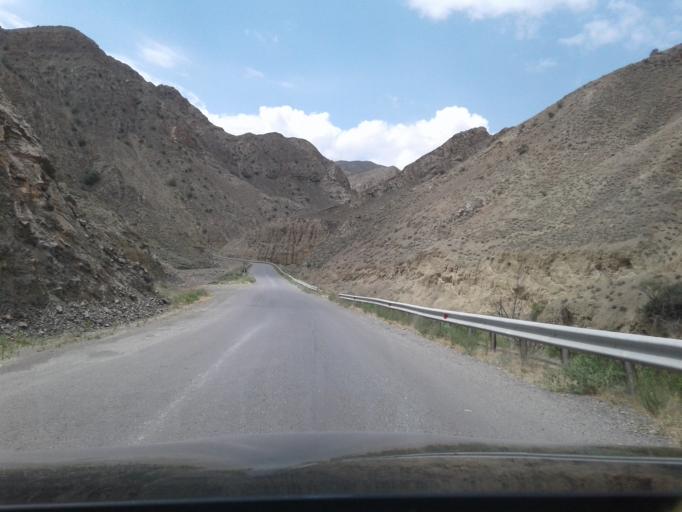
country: TM
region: Ahal
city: Baharly
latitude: 38.5052
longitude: 57.0507
